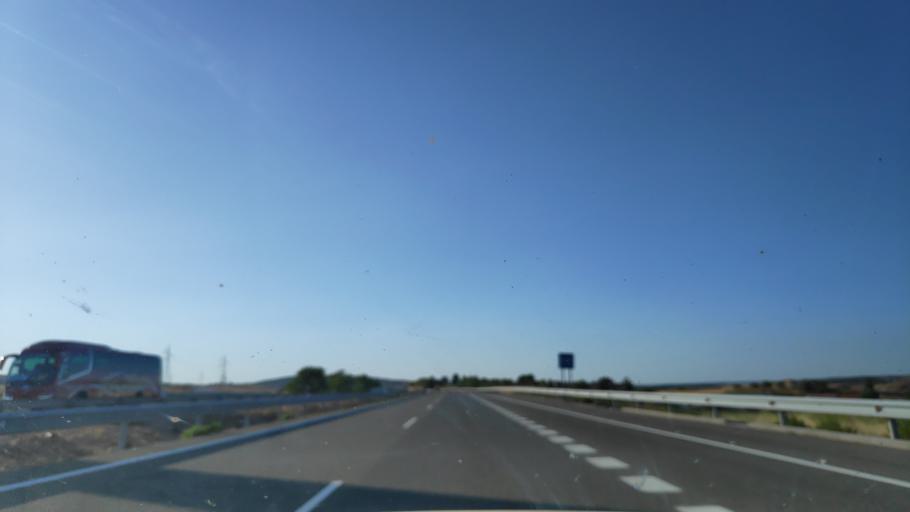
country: ES
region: Castille-La Mancha
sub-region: Provincia de Cuenca
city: Villares del Saz
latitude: 39.8394
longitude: -2.5131
